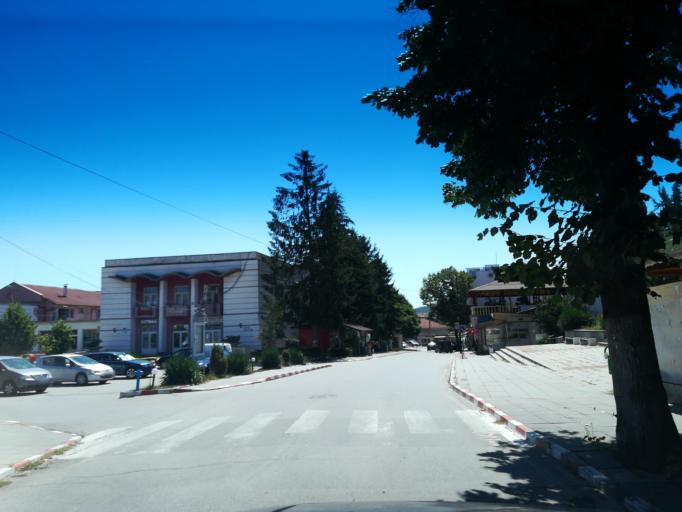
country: BG
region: Pazardzhik
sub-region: Obshtina Strelcha
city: Strelcha
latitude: 42.5065
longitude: 24.3209
